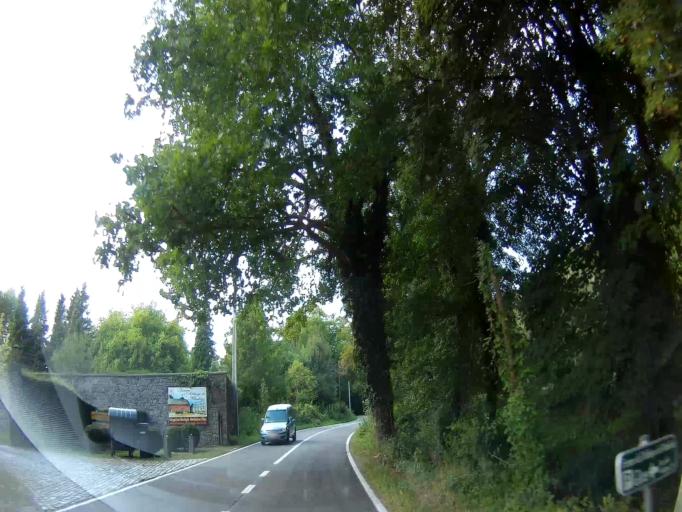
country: BE
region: Wallonia
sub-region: Province de Namur
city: Anhee
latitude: 50.3173
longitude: 4.8610
